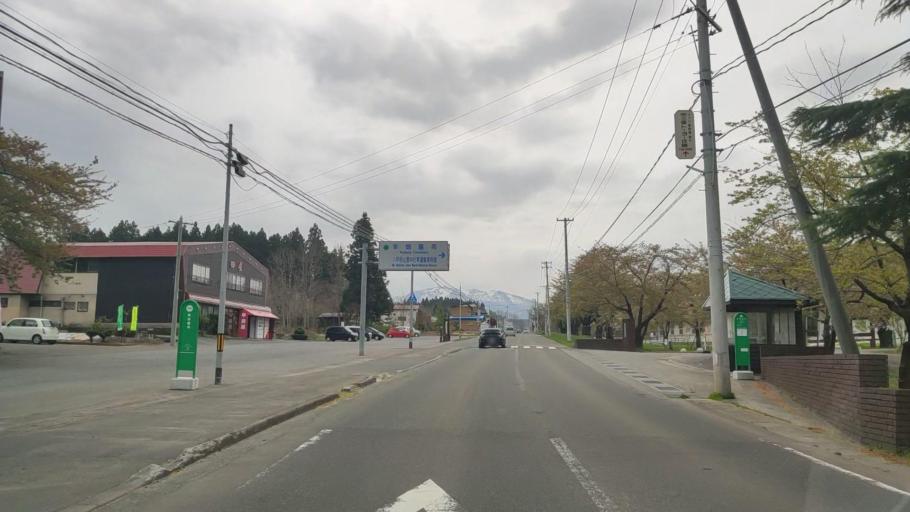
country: JP
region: Aomori
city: Aomori Shi
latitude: 40.7855
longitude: 140.7897
